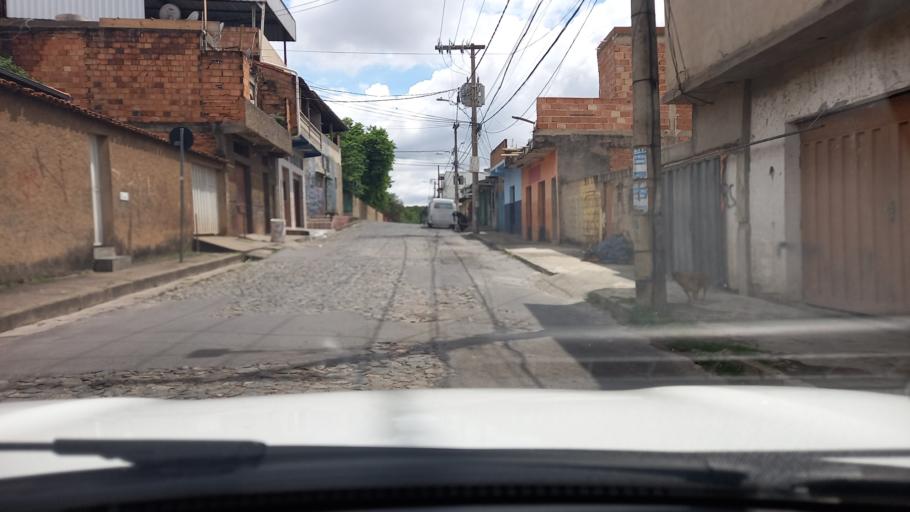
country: BR
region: Minas Gerais
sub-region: Contagem
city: Contagem
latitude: -19.9011
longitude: -44.0251
